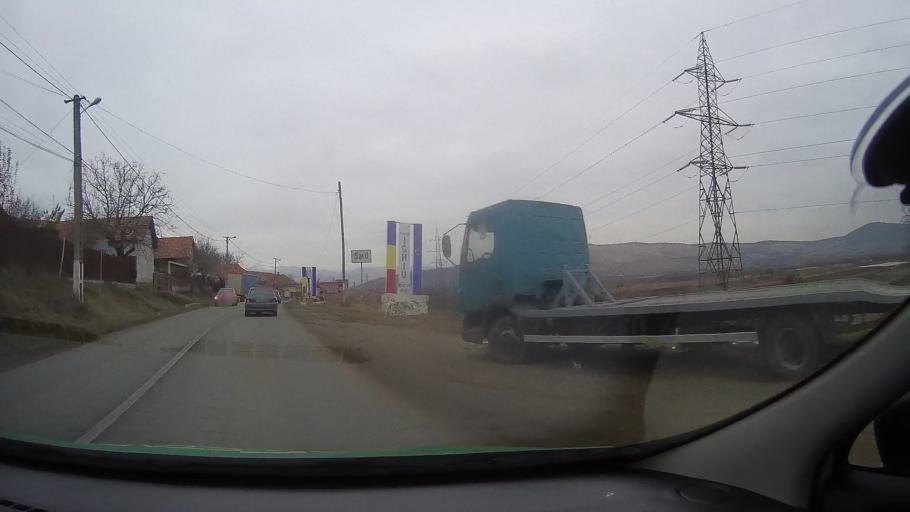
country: RO
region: Alba
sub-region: Comuna Ighiu
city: Sard
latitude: 46.1153
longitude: 23.5385
